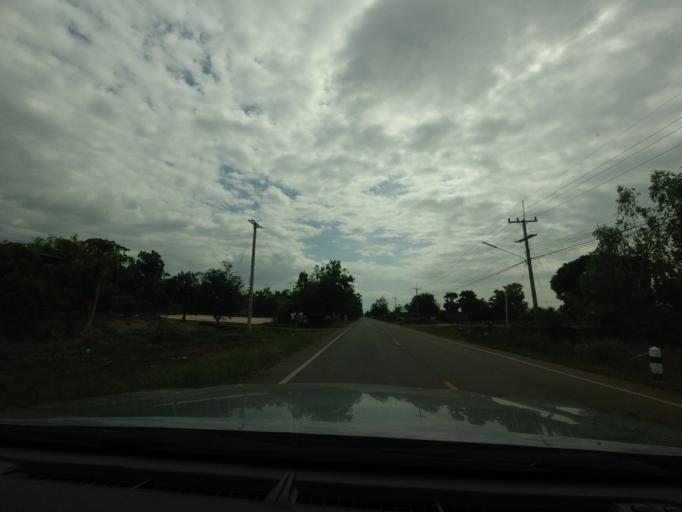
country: TH
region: Phitsanulok
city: Noen Maprang
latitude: 16.6069
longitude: 100.6206
